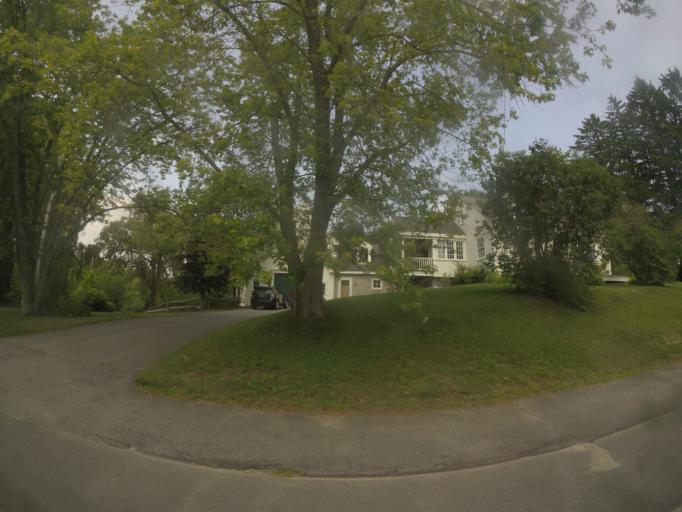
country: US
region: Maine
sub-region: Cumberland County
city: Falmouth
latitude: 43.7209
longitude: -70.2305
